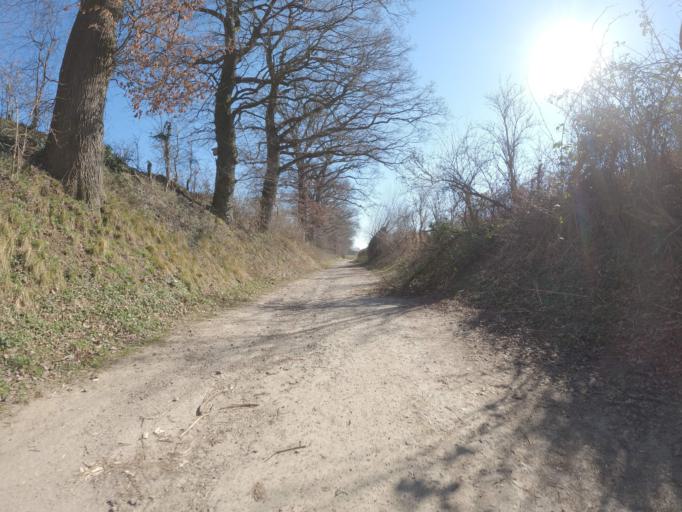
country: NL
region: Limburg
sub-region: Gemeente Kerkrade
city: Kerkrade
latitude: 50.8330
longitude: 6.0296
